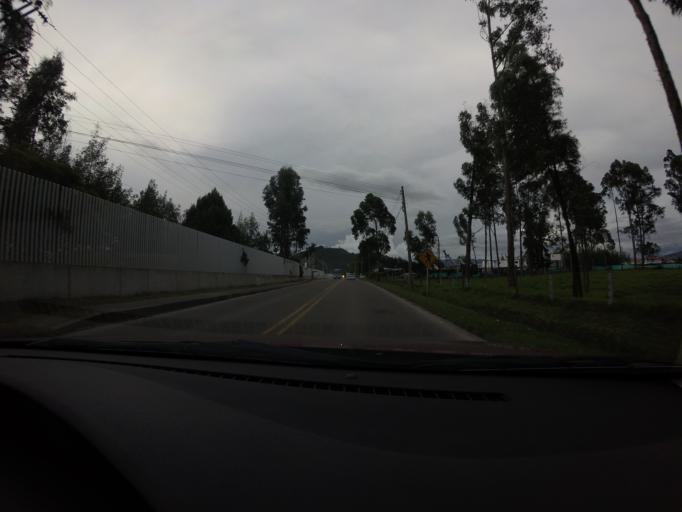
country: CO
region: Cundinamarca
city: Sopo
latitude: 4.9329
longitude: -73.9540
